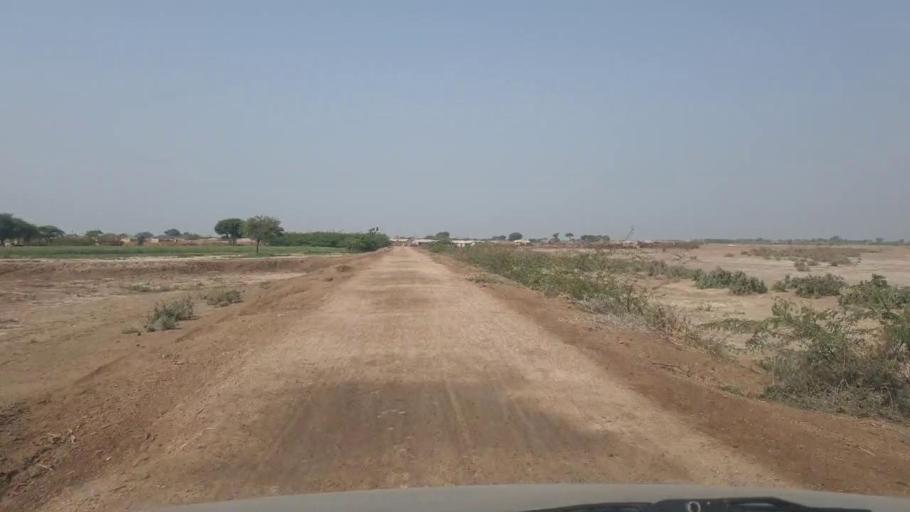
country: PK
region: Sindh
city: Chor
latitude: 25.4653
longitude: 69.7402
